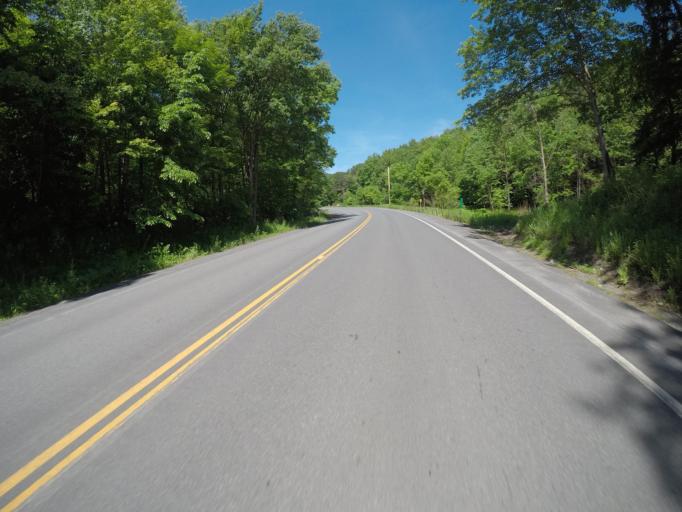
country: US
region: New York
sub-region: Delaware County
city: Delhi
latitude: 42.2579
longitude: -74.9518
